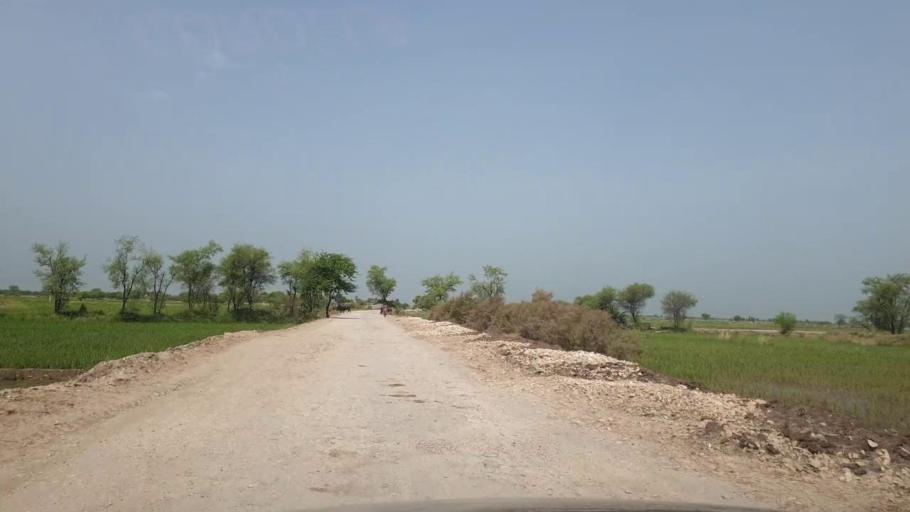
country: PK
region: Sindh
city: Garhi Yasin
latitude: 27.8558
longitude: 68.4212
